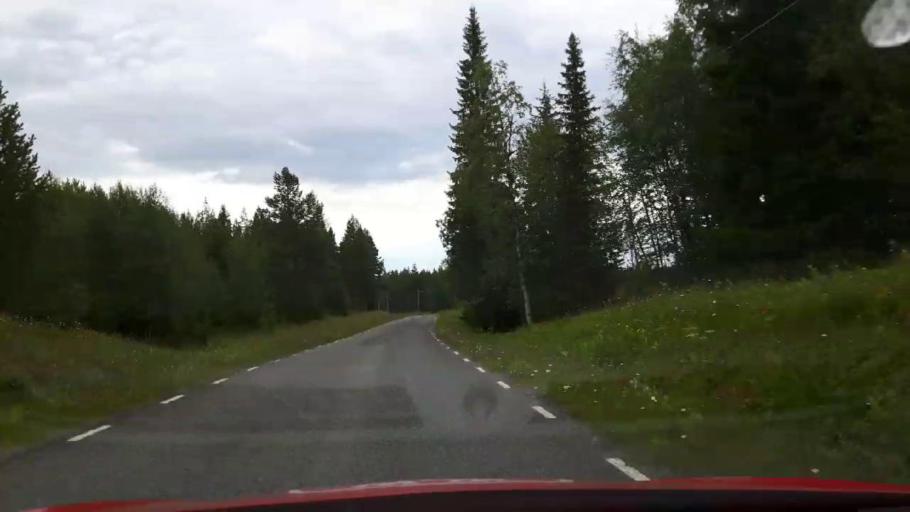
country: SE
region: Jaemtland
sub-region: OEstersunds Kommun
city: Lit
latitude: 63.3839
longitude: 15.0371
